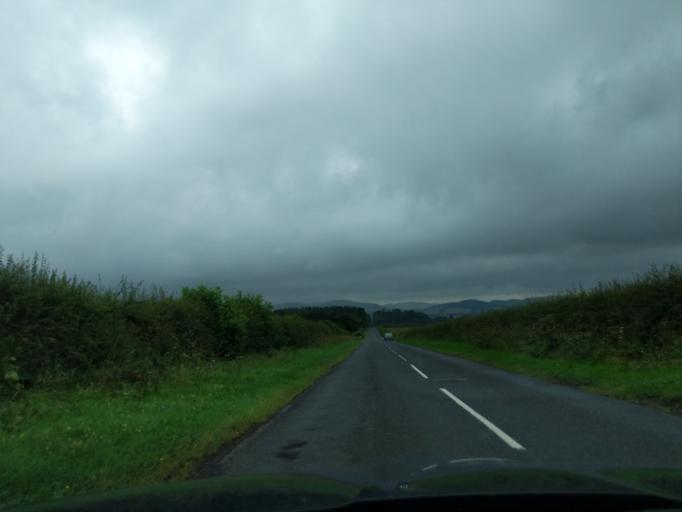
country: GB
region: England
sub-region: Northumberland
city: Ford
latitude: 55.6384
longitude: -2.0689
